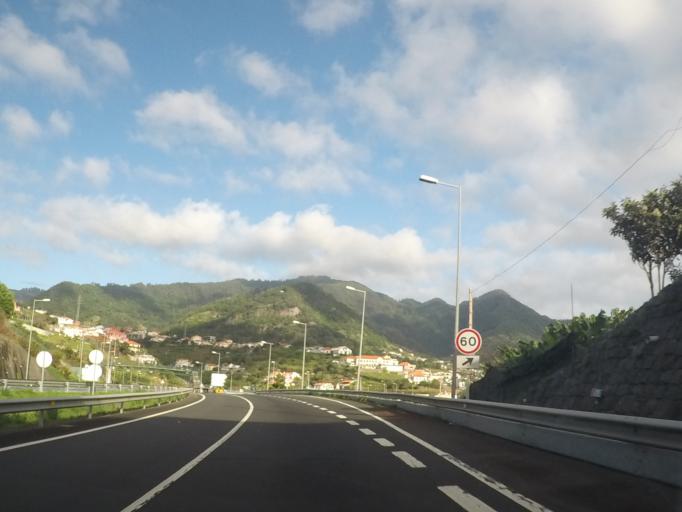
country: PT
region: Madeira
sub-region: Machico
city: Machico
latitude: 32.7257
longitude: -16.7779
